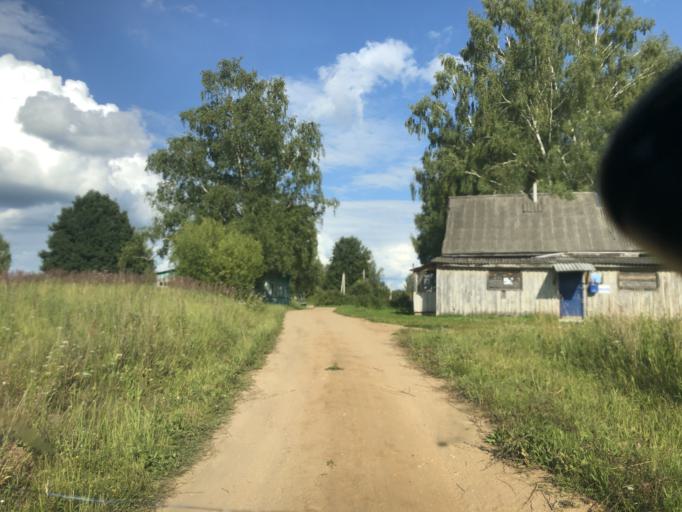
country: RU
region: Smolensk
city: Ugra
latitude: 54.8501
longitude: 34.5040
